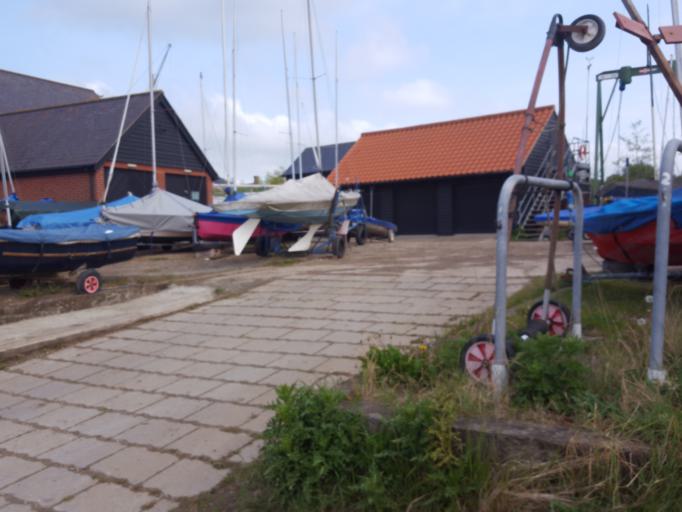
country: GB
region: England
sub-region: Essex
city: Wivenhoe
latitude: 51.8526
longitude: 0.9647
